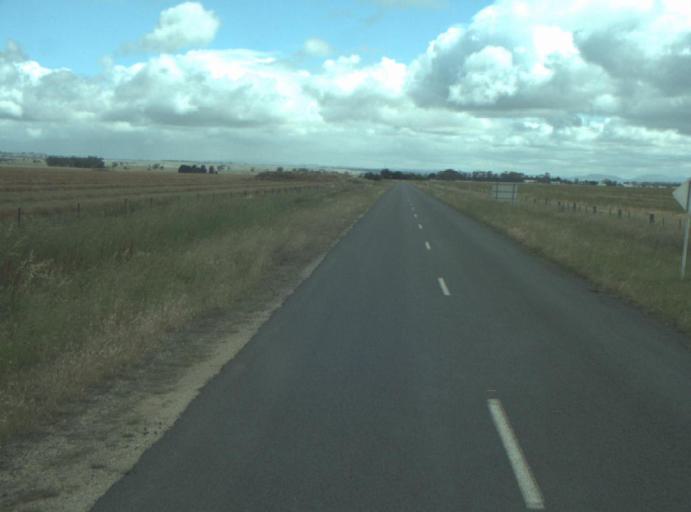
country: AU
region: Victoria
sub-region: Moorabool
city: Bacchus Marsh
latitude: -37.8333
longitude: 144.3567
